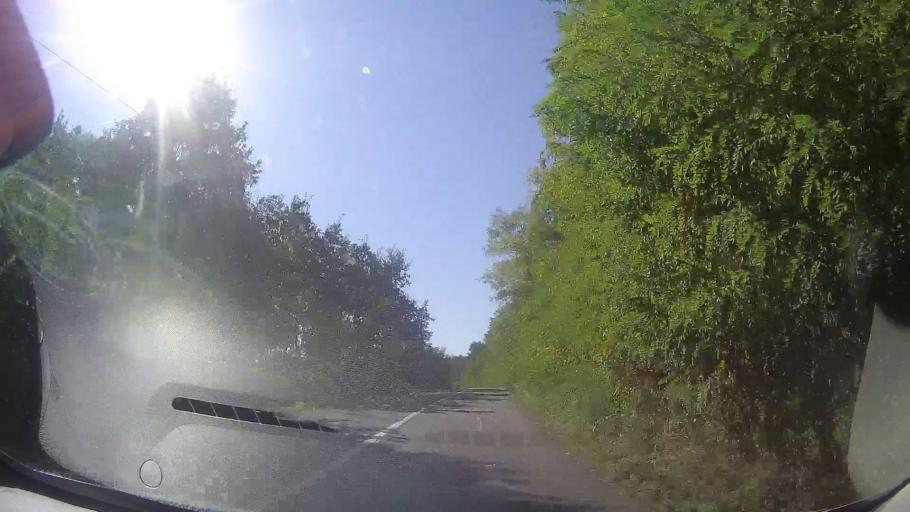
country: RO
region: Timis
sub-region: Comuna Ohaba Lunga
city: Ohaba Lunga
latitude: 45.8868
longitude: 21.9675
